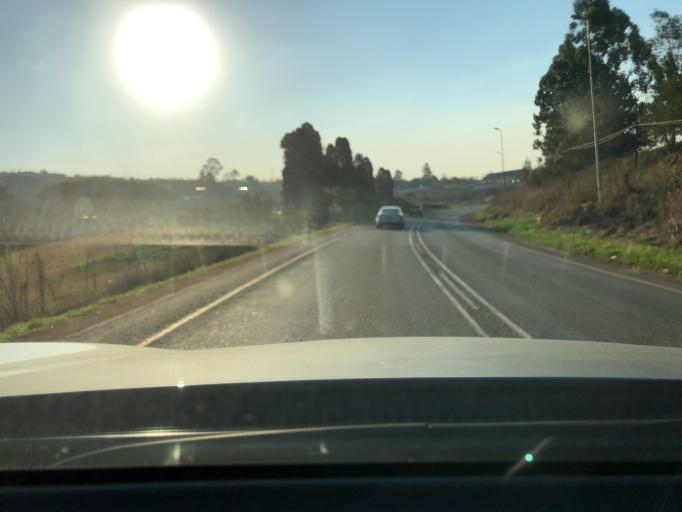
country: ZA
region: KwaZulu-Natal
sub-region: Sisonke District Municipality
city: Ixopo
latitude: -30.1534
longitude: 30.0762
